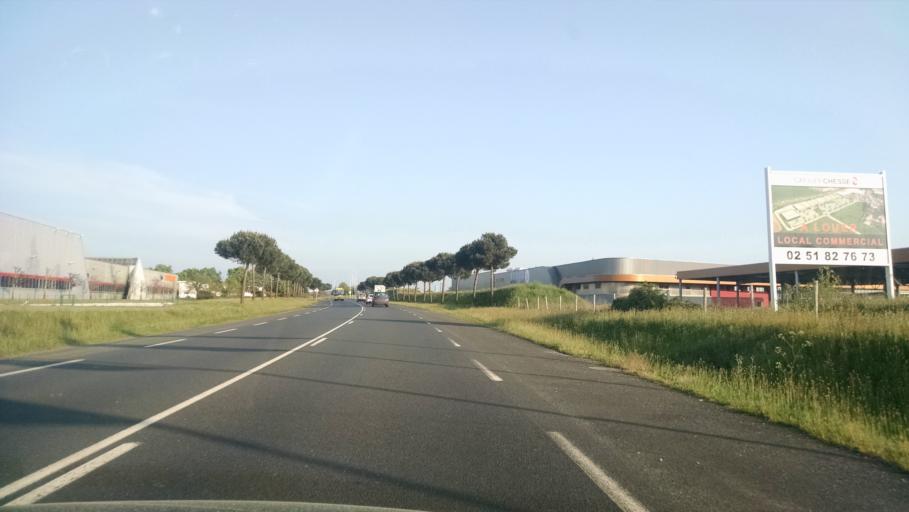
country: FR
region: Pays de la Loire
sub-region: Departement de la Loire-Atlantique
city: Getigne
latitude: 47.0866
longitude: -1.2614
